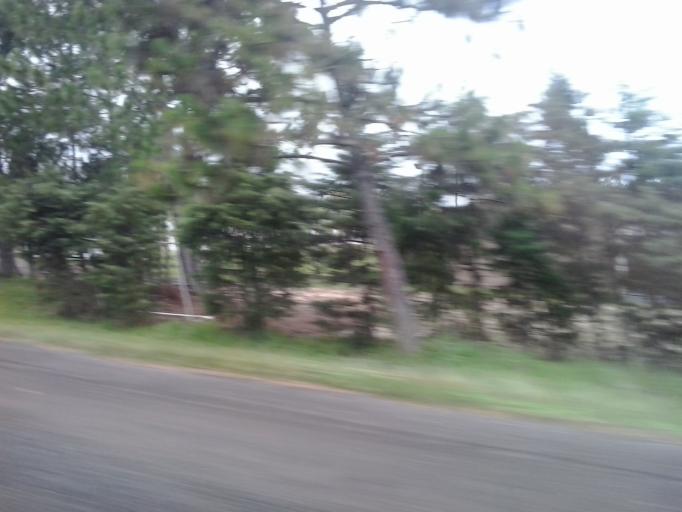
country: BR
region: Rio Grande do Sul
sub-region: Candelaria
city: Candelaria
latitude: -29.7153
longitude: -53.2475
